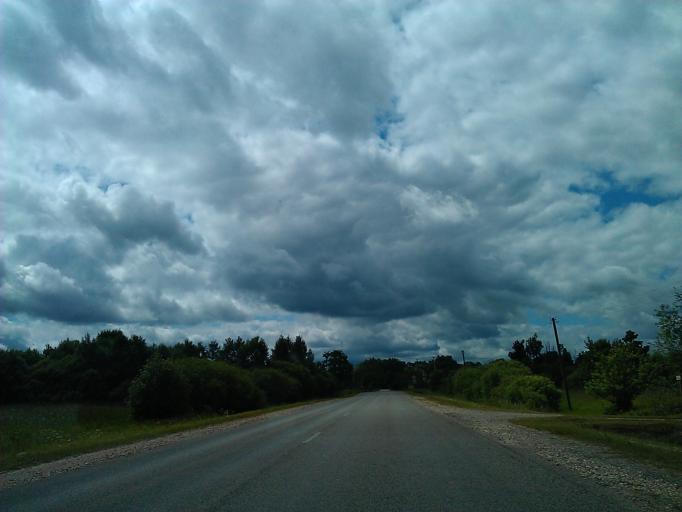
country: LV
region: Talsu Rajons
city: Stende
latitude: 57.0792
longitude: 22.2940
